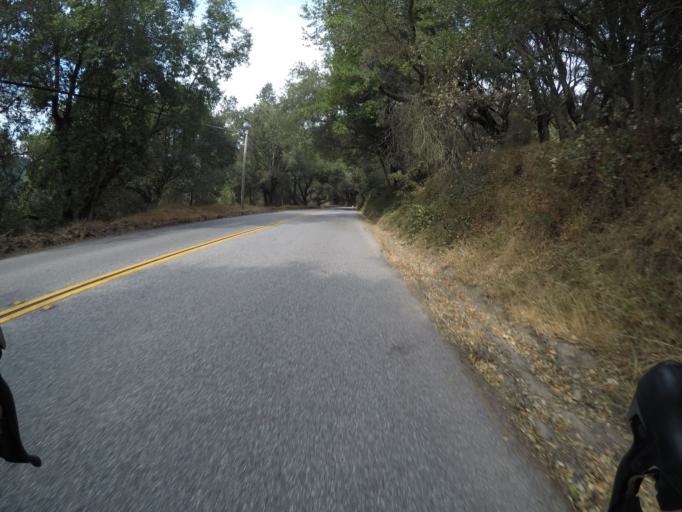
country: US
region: California
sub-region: Santa Cruz County
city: Scotts Valley
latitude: 37.0851
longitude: -122.0058
